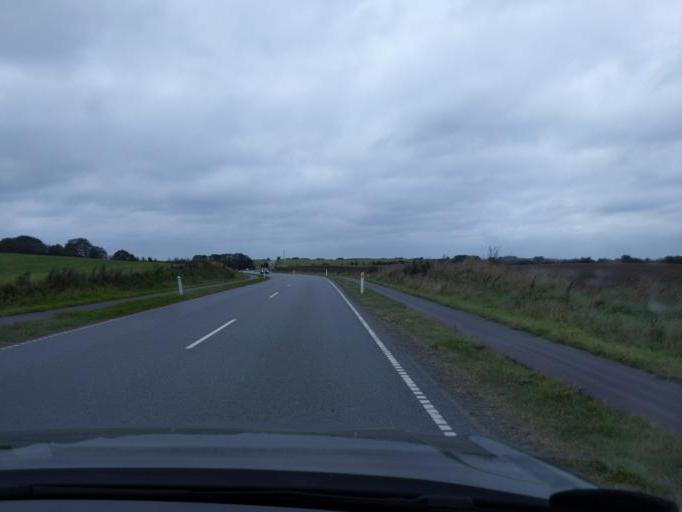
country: DK
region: North Denmark
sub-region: Mariagerfjord Kommune
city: Hobro
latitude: 56.5983
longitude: 9.7900
